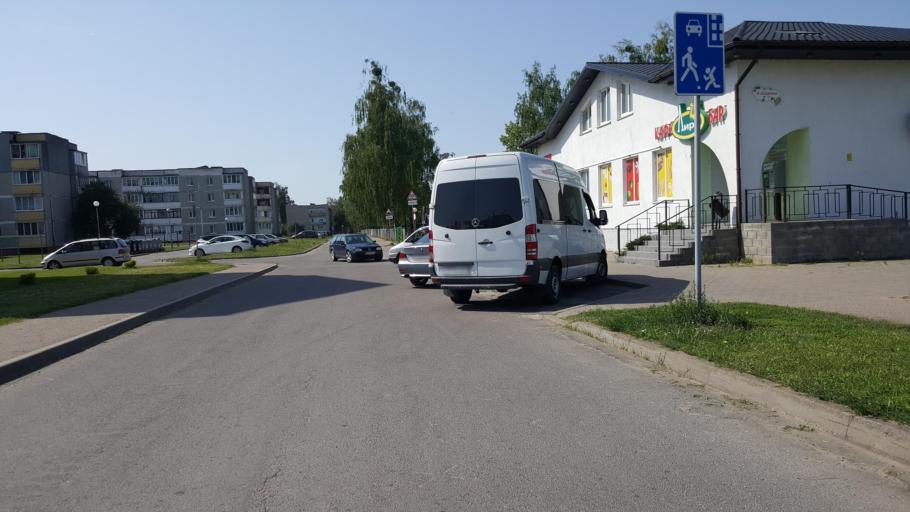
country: BY
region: Brest
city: Zhabinka
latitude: 52.1907
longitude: 24.0342
